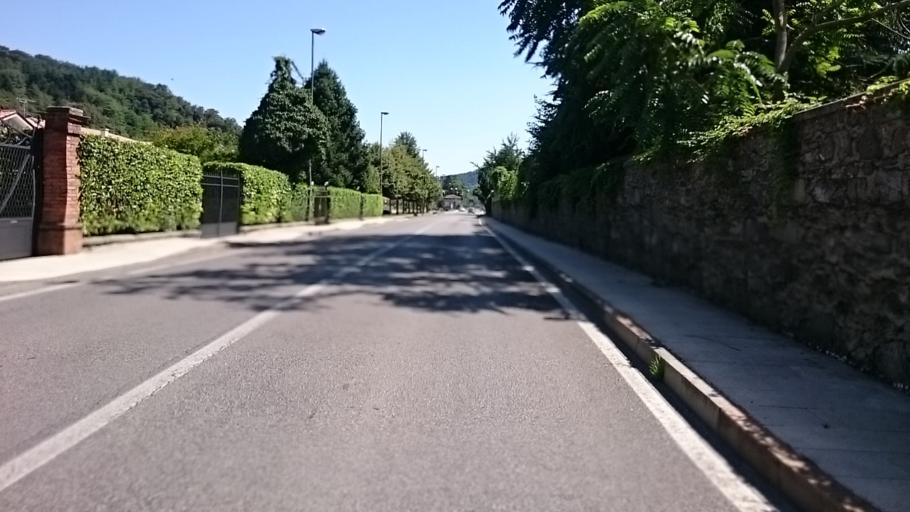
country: IT
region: Veneto
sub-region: Provincia di Treviso
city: Follina
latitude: 45.9504
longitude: 12.1206
